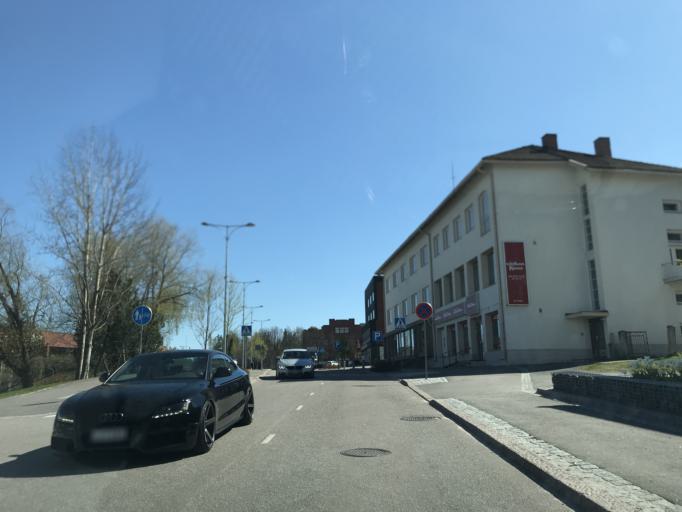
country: FI
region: Paijanne Tavastia
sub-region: Lahti
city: Orimattila
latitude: 60.8032
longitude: 25.7339
